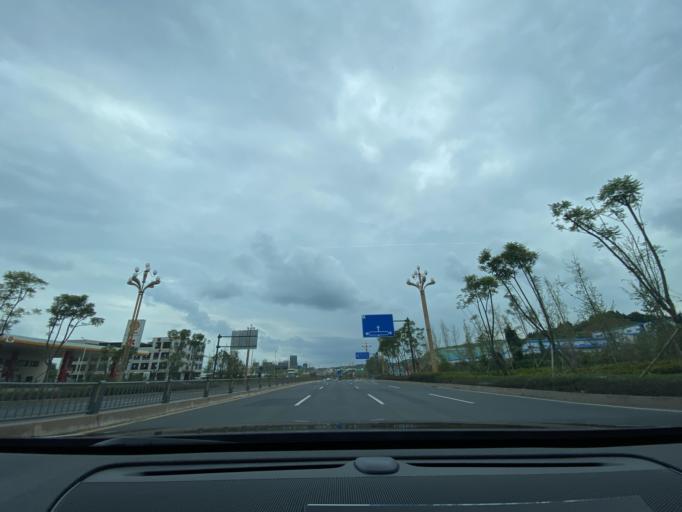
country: CN
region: Sichuan
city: Jiancheng
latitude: 30.4480
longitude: 104.4959
